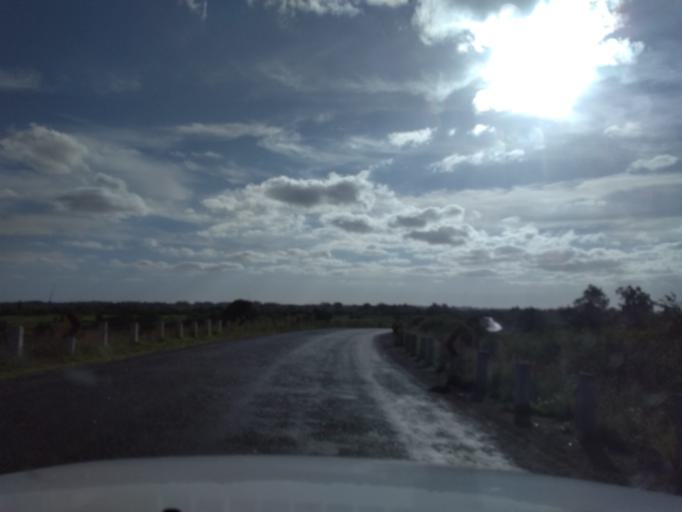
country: UY
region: Canelones
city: San Ramon
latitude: -34.2667
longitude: -55.9296
